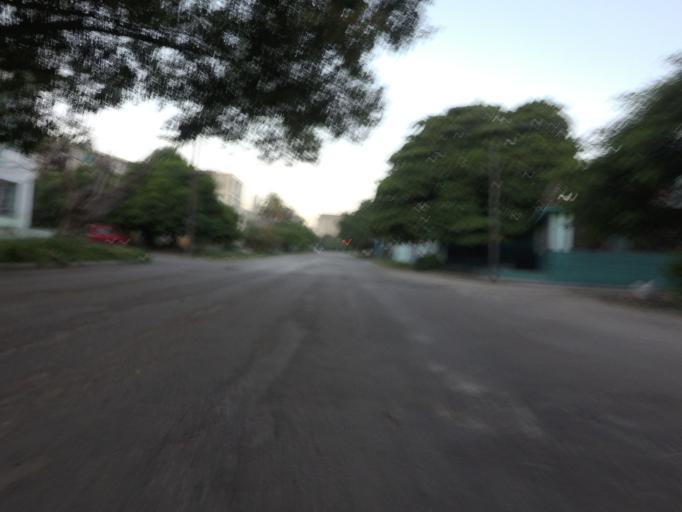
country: CU
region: La Habana
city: Havana
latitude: 23.1235
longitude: -82.3792
